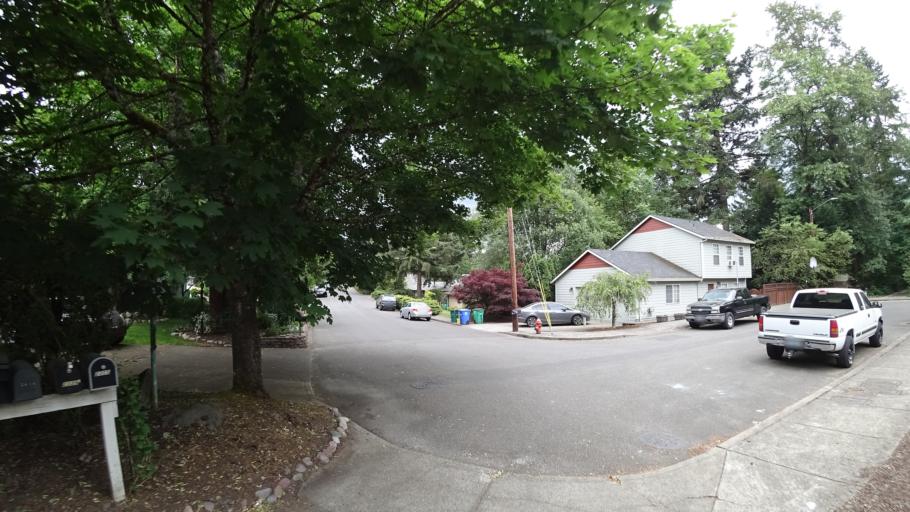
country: US
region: Oregon
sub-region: Clackamas County
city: Lake Oswego
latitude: 45.4605
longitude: -122.7013
